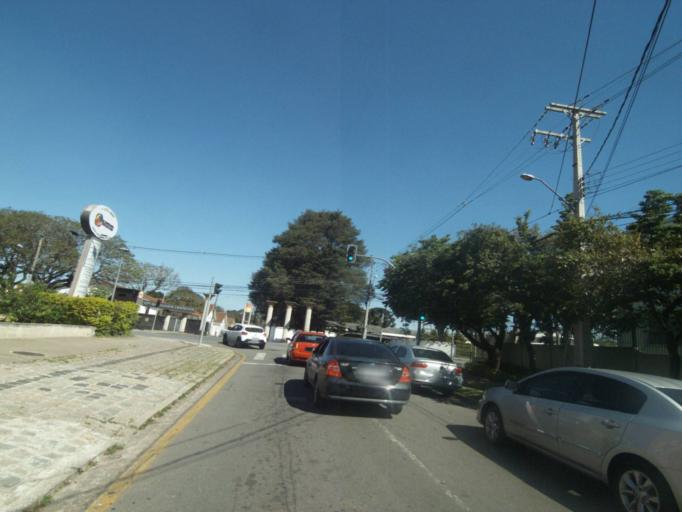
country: BR
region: Parana
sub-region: Curitiba
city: Curitiba
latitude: -25.3952
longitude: -49.2311
